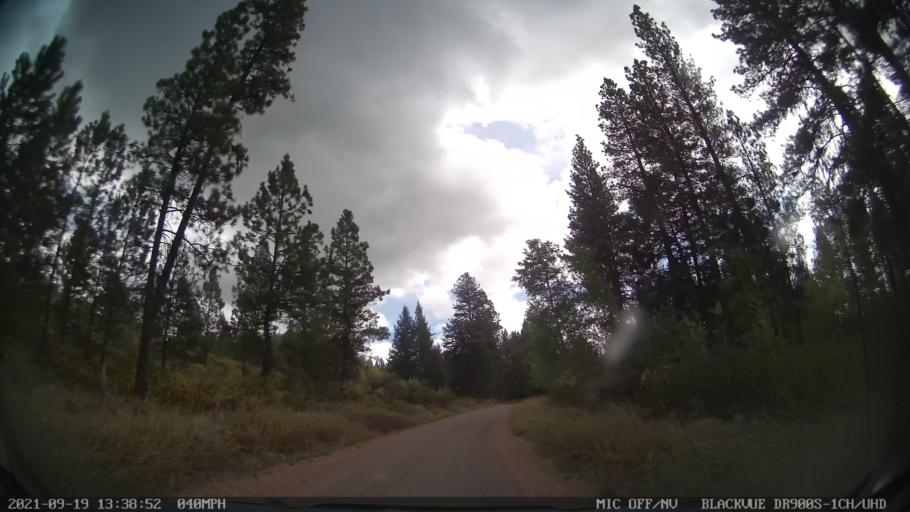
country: US
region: Montana
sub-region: Missoula County
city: Seeley Lake
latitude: 47.1023
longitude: -113.2674
